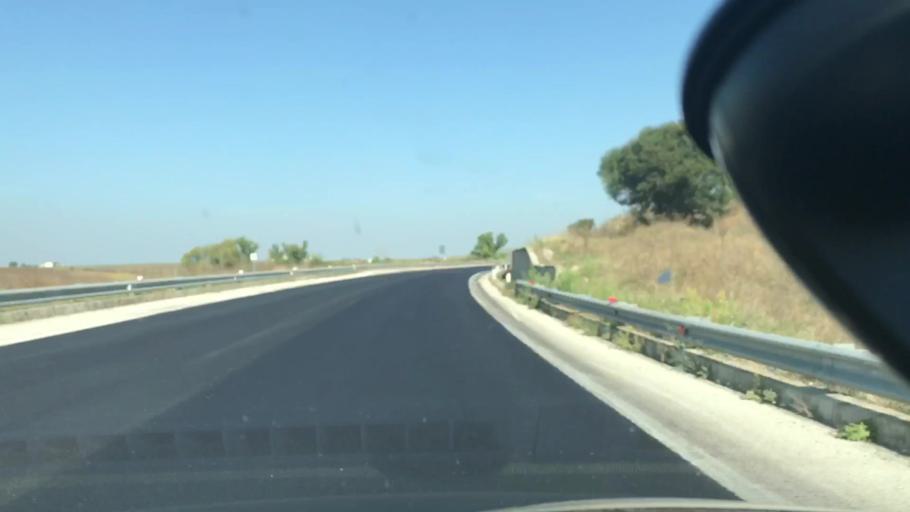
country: IT
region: Apulia
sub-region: Provincia di Barletta - Andria - Trani
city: Spinazzola
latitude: 40.9077
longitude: 16.1089
